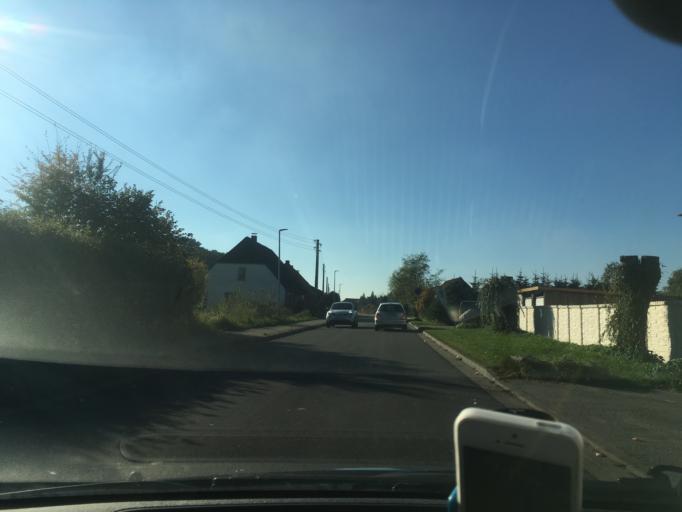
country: DE
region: Mecklenburg-Vorpommern
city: Dummer
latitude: 53.5664
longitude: 11.2140
